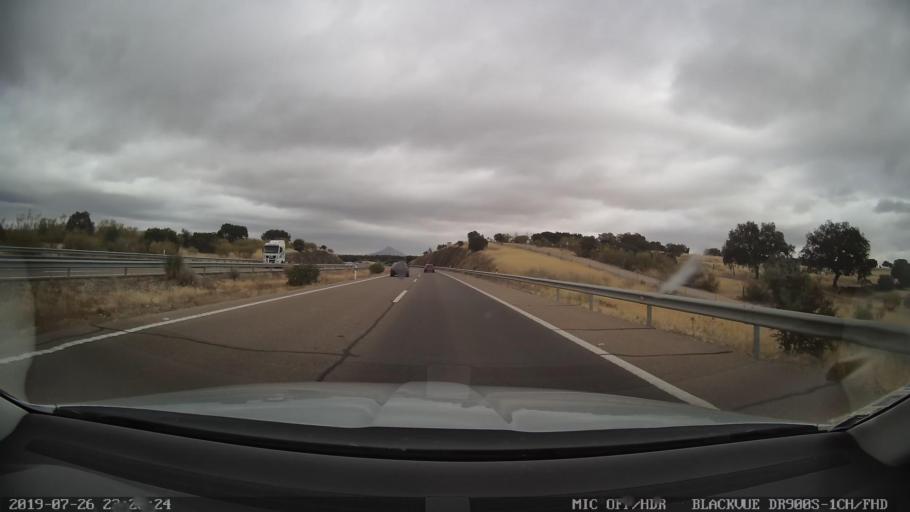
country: ES
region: Extremadura
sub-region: Provincia de Caceres
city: Escurial
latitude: 39.2068
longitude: -5.8780
